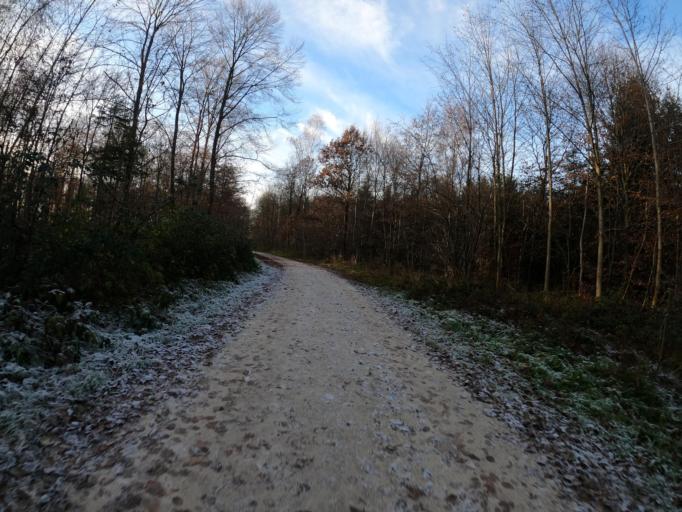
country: DE
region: Baden-Wuerttemberg
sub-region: Regierungsbezirk Stuttgart
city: Albershausen
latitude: 48.6783
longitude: 9.5494
